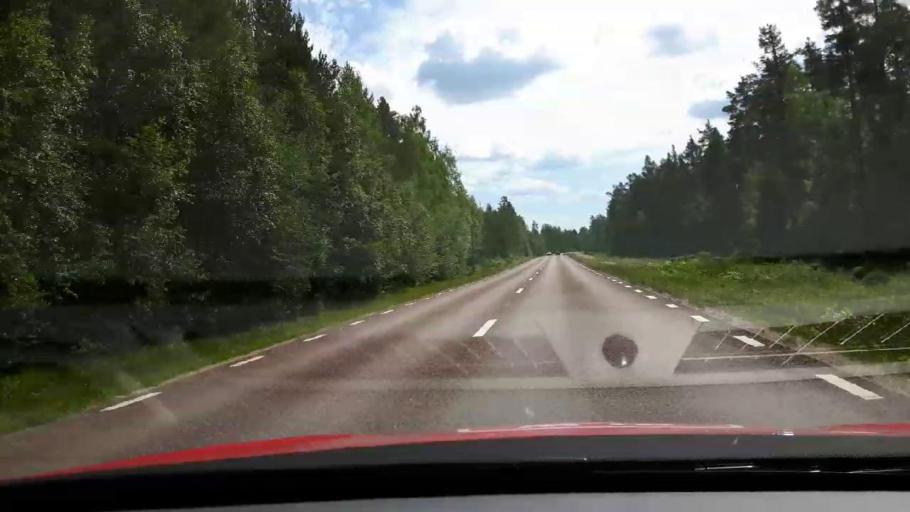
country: SE
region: Jaemtland
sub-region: Harjedalens Kommun
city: Sveg
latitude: 62.1402
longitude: 14.9627
